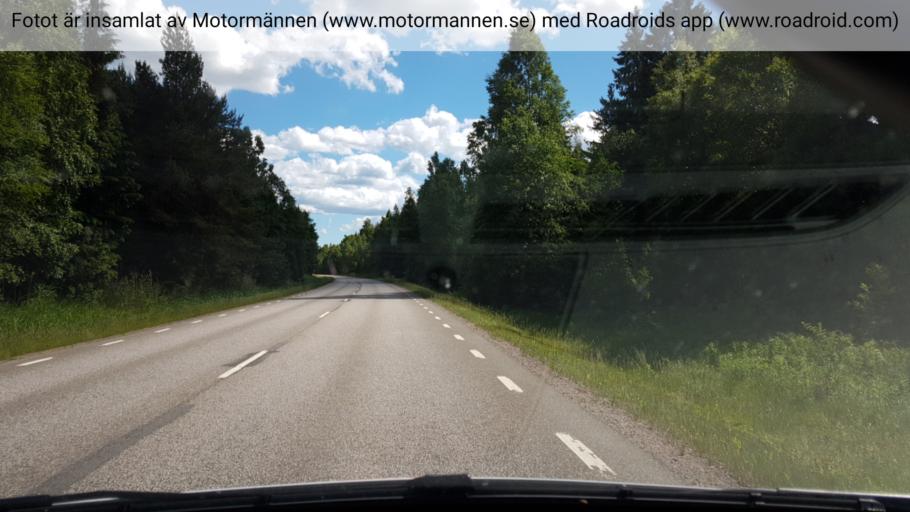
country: SE
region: Vaestra Goetaland
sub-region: Tibro Kommun
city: Tibro
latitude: 58.3672
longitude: 14.2079
